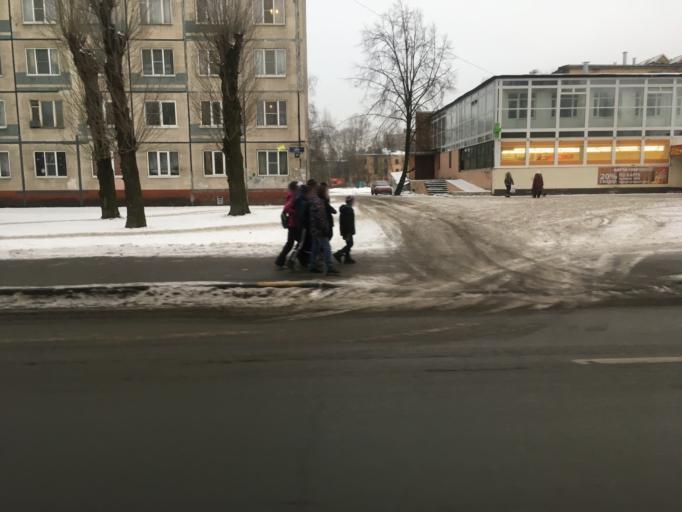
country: RU
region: St.-Petersburg
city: Obukhovo
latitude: 59.8652
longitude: 30.4445
